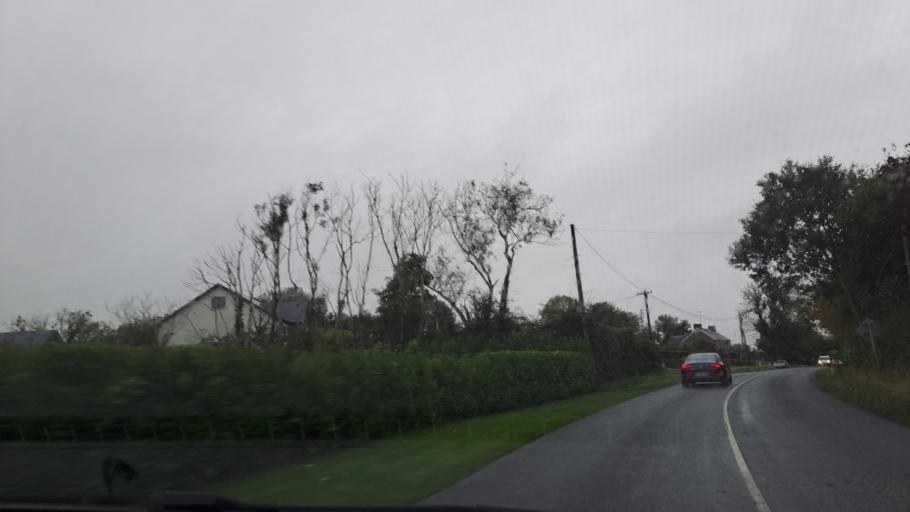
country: IE
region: Ulster
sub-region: County Monaghan
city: Monaghan
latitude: 54.2186
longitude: -6.9172
